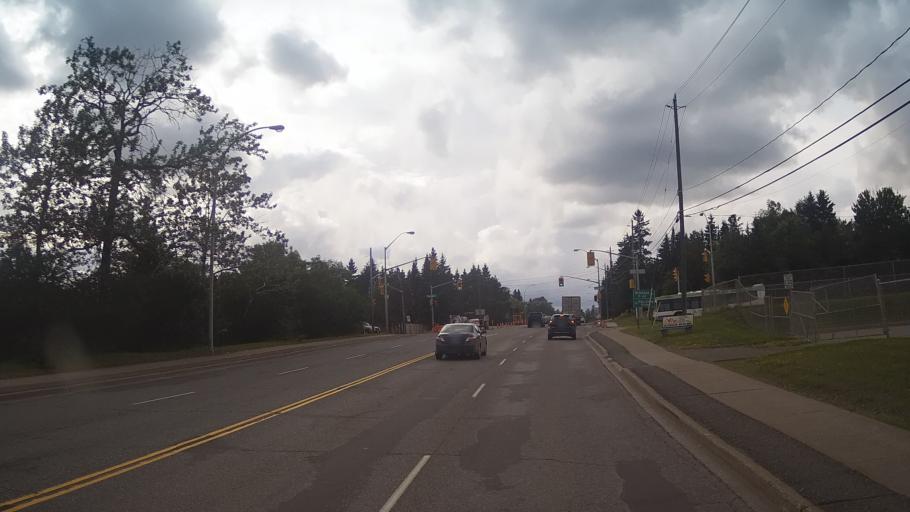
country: CA
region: Ontario
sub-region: Thunder Bay District
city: Thunder Bay
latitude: 48.4533
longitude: -89.2586
